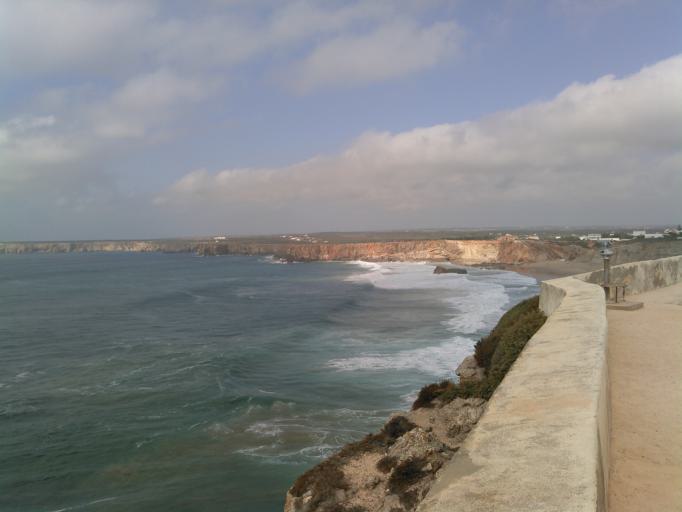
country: PT
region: Faro
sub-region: Vila do Bispo
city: Sagres
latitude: 37.0005
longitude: -8.9496
